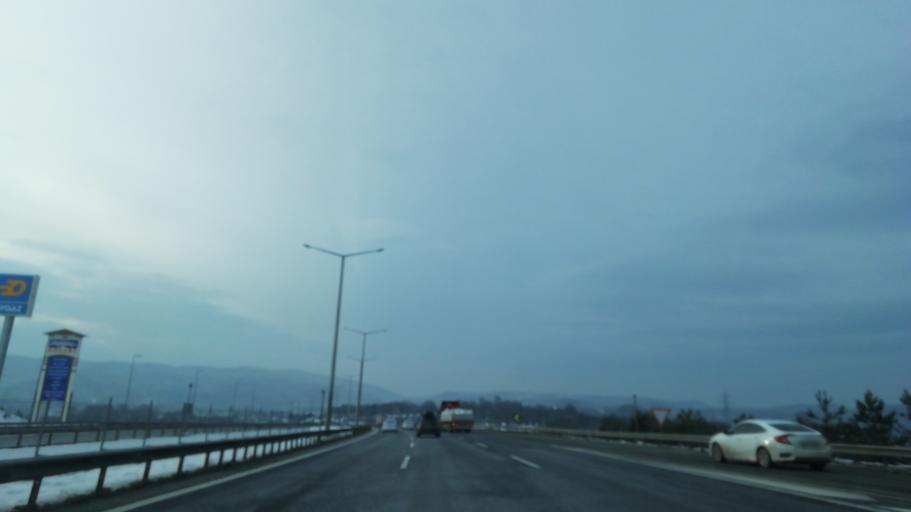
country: TR
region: Bolu
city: Bolu
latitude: 40.7252
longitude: 31.4616
